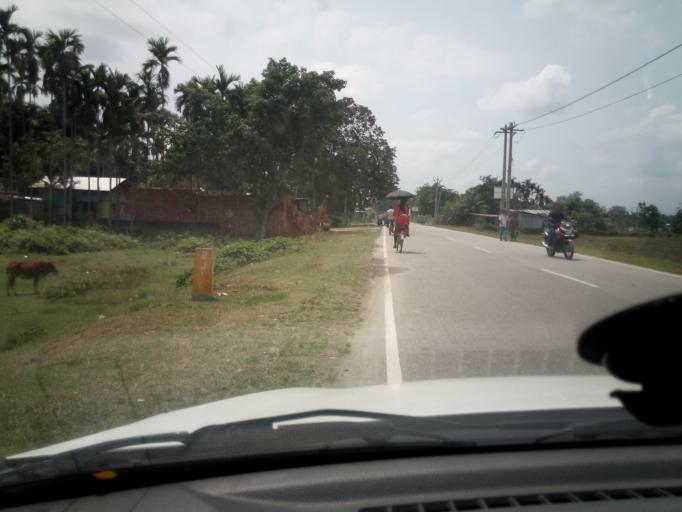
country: IN
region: Assam
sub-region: Udalguri
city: Udalguri
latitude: 26.7144
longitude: 92.2016
